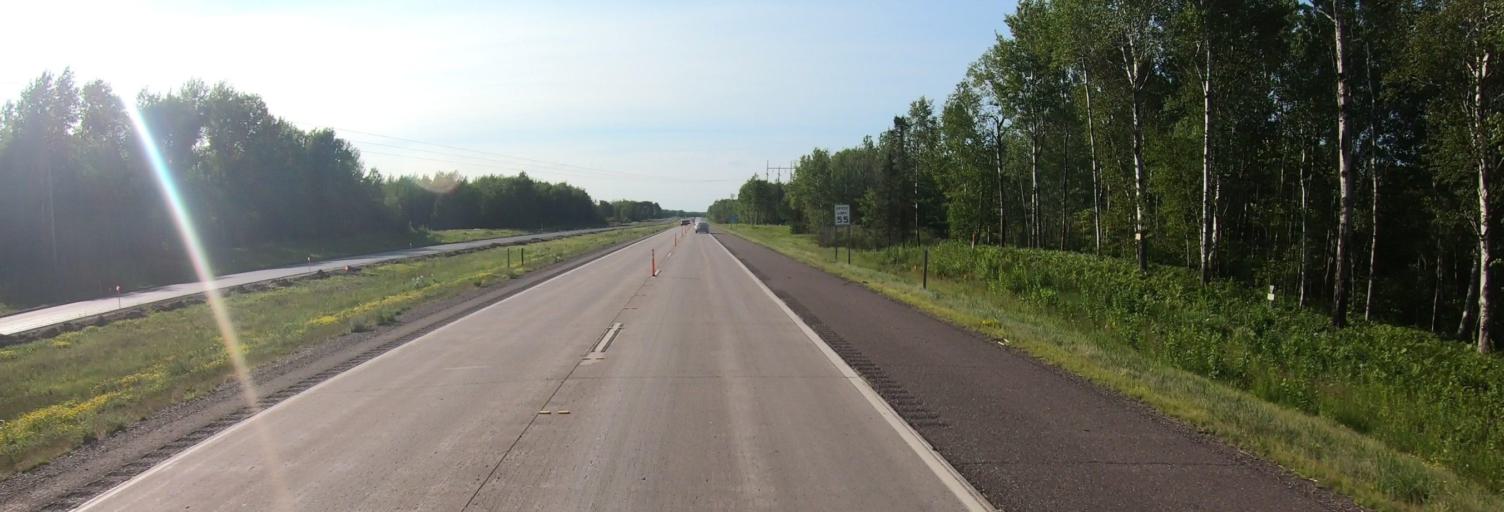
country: US
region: Minnesota
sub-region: Saint Louis County
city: Hermantown
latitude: 46.9041
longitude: -92.3796
